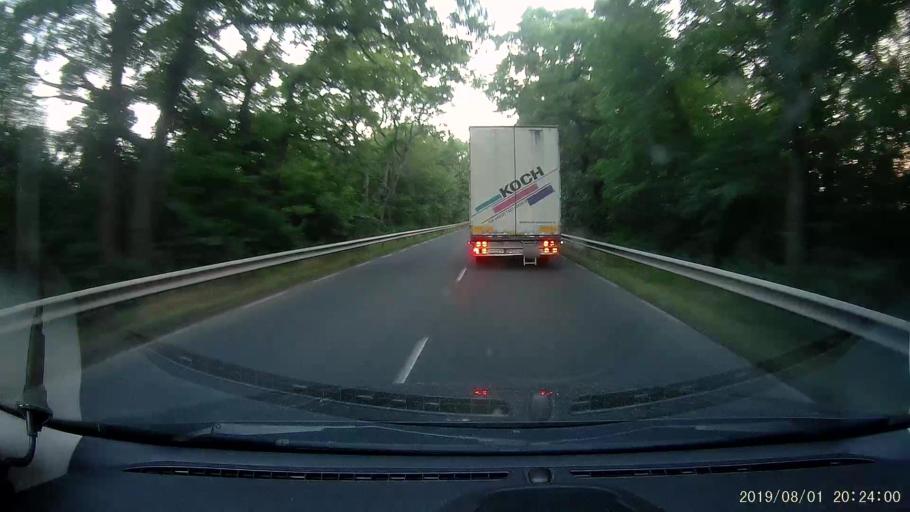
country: BG
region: Yambol
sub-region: Obshtina Elkhovo
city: Elkhovo
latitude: 42.2383
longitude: 26.5962
